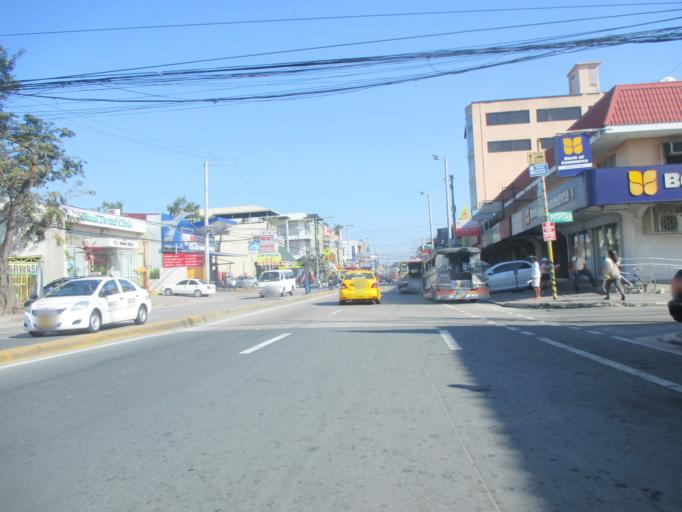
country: PH
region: Metro Manila
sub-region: Marikina
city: Calumpang
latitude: 14.6214
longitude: 121.1019
